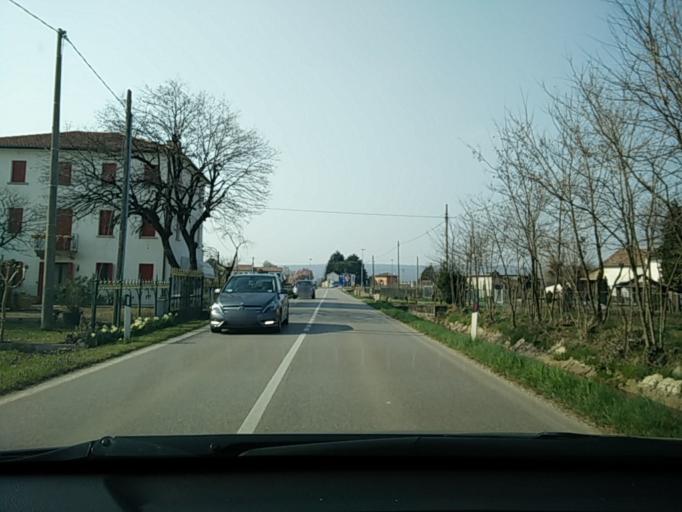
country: IT
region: Veneto
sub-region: Provincia di Treviso
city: Camalo
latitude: 45.7612
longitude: 12.1591
